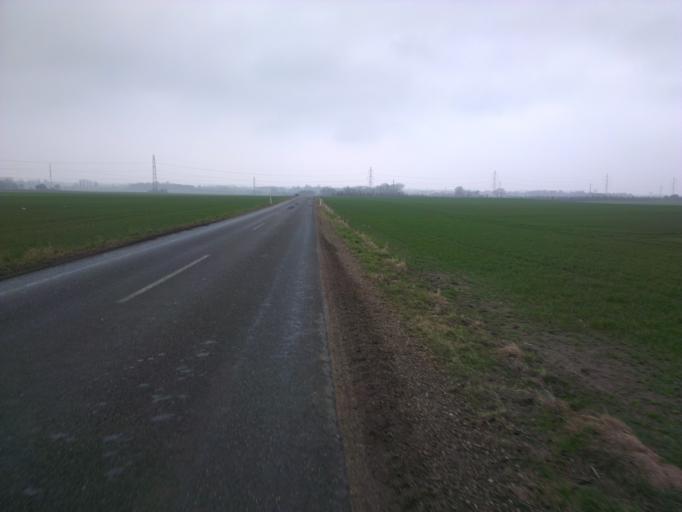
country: DK
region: Capital Region
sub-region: Frederikssund Kommune
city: Skibby
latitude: 55.7970
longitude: 11.9589
